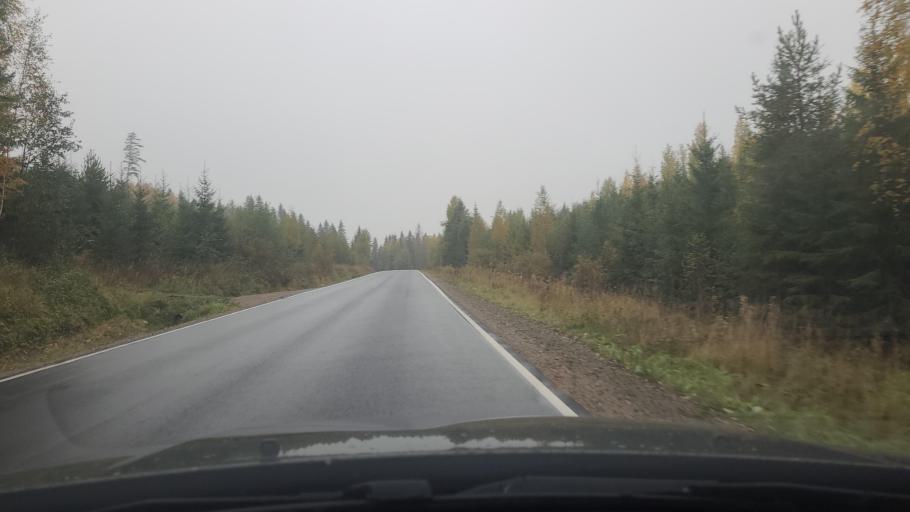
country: FI
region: Northern Savo
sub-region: Varkaus
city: Kangaslampi
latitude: 62.4582
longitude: 28.2668
